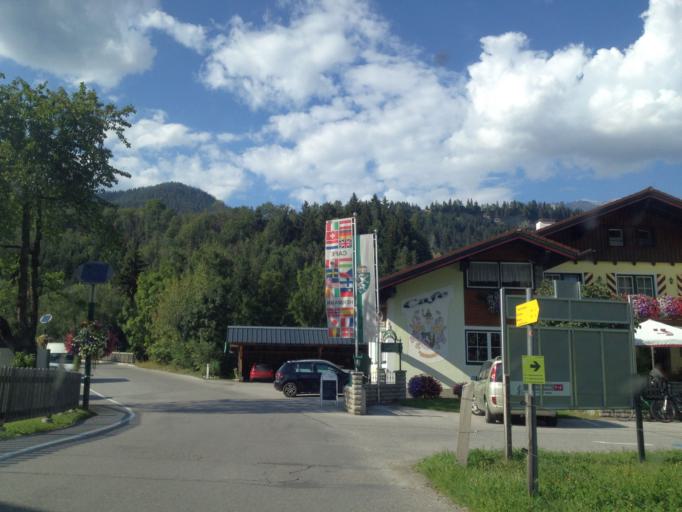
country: AT
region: Styria
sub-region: Politischer Bezirk Liezen
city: Schladming
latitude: 47.3874
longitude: 13.6175
